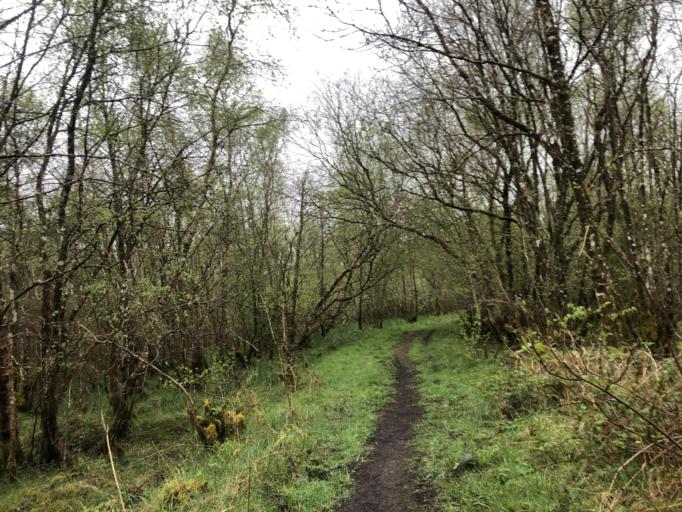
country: IE
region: Connaught
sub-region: County Leitrim
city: Carrick-on-Shannon
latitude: 53.9889
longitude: -8.1855
